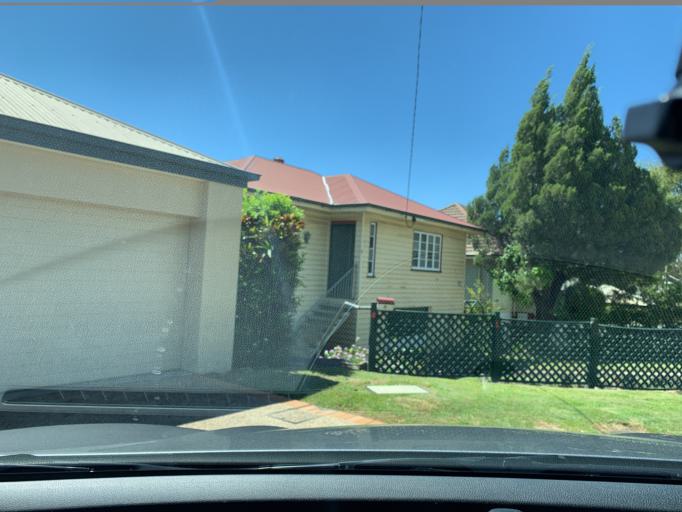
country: AU
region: Queensland
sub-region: Brisbane
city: Ascot
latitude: -27.4210
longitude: 153.0646
